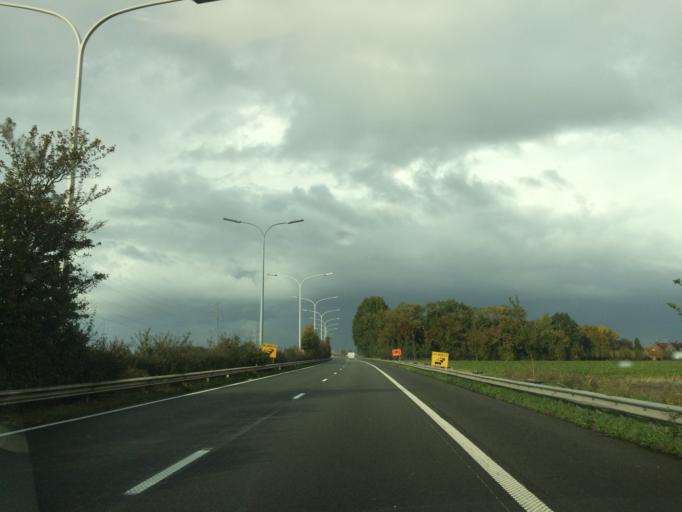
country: BE
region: Flanders
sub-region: Provincie West-Vlaanderen
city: Zuienkerke
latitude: 51.2366
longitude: 3.1884
